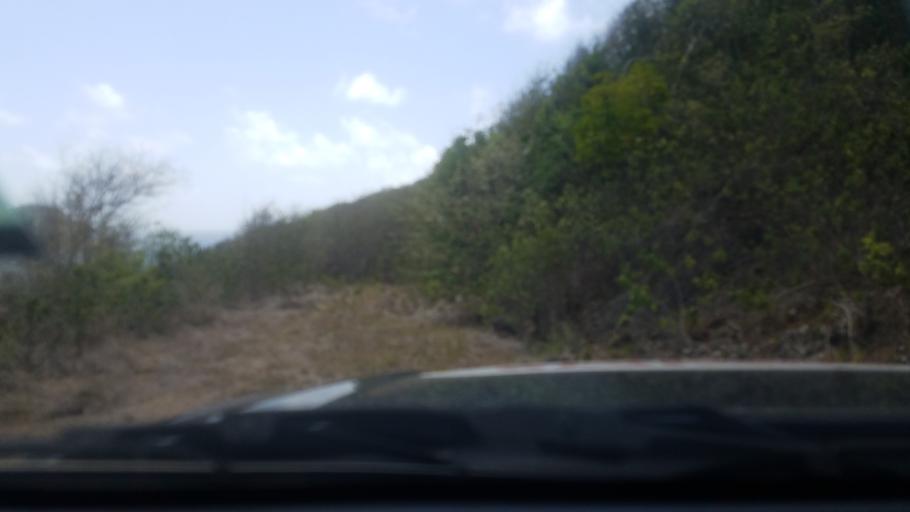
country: LC
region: Vieux-Fort
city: Vieux Fort
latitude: 13.7207
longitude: -60.9480
